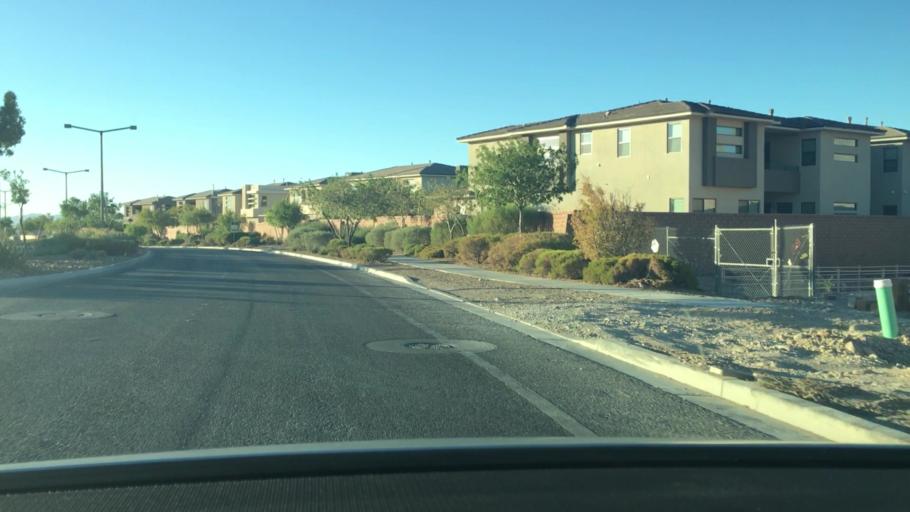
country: US
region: Nevada
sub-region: Clark County
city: Summerlin South
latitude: 36.1178
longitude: -115.3351
